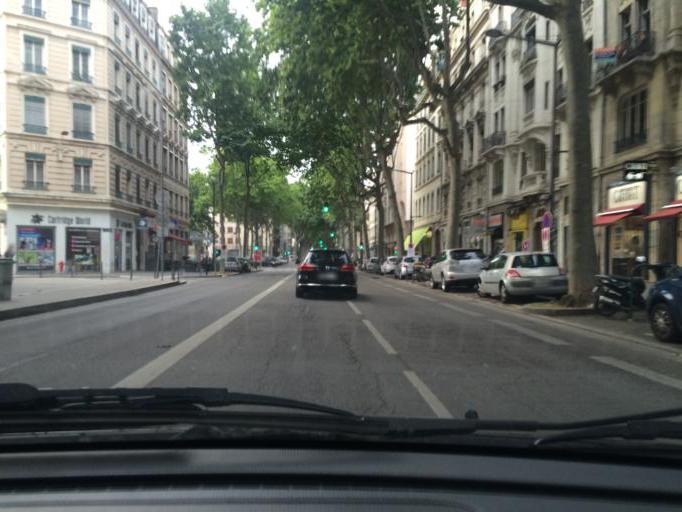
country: FR
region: Rhone-Alpes
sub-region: Departement du Rhone
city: Lyon
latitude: 45.7566
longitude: 4.8464
